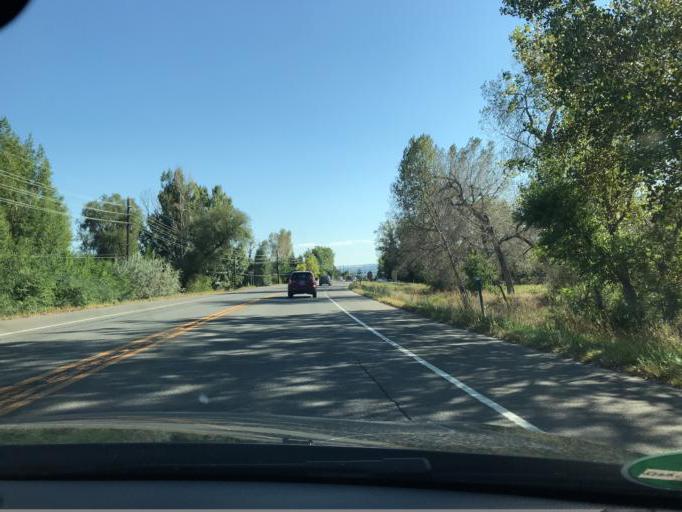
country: US
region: Colorado
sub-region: Boulder County
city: Boulder
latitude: 40.0481
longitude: -105.2588
